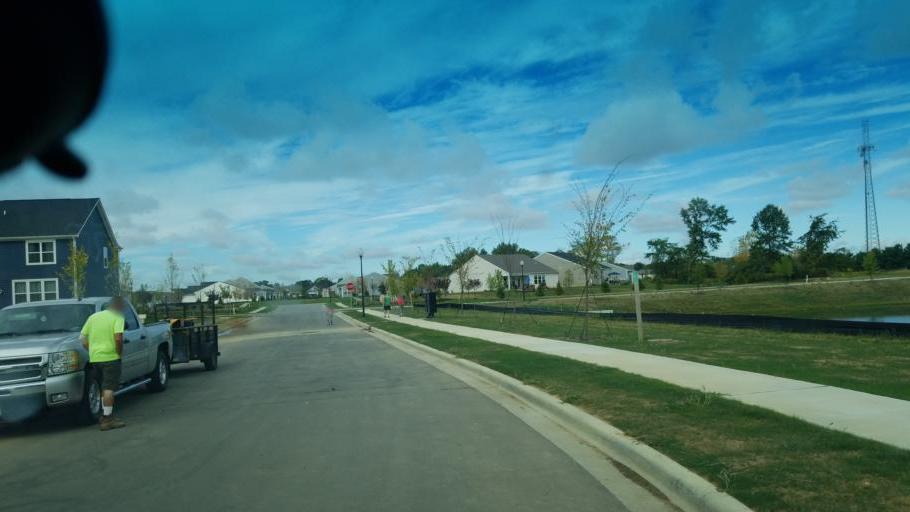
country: US
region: Ohio
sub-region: Delaware County
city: Sunbury
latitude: 40.2388
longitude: -82.8641
